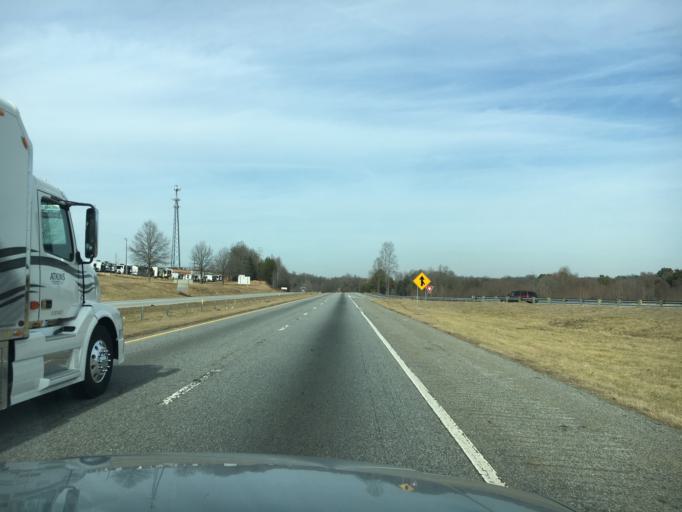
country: US
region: South Carolina
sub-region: Spartanburg County
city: Boiling Springs
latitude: 35.0280
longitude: -82.0351
